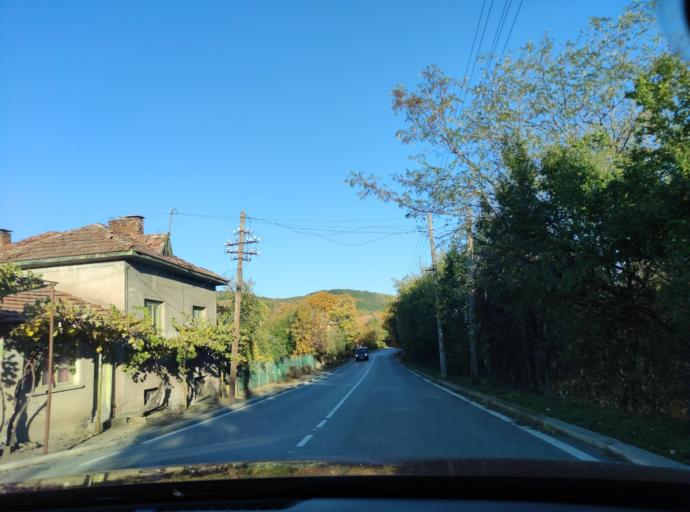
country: BG
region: Montana
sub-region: Obshtina Chiprovtsi
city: Chiprovtsi
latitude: 43.4341
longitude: 22.9676
